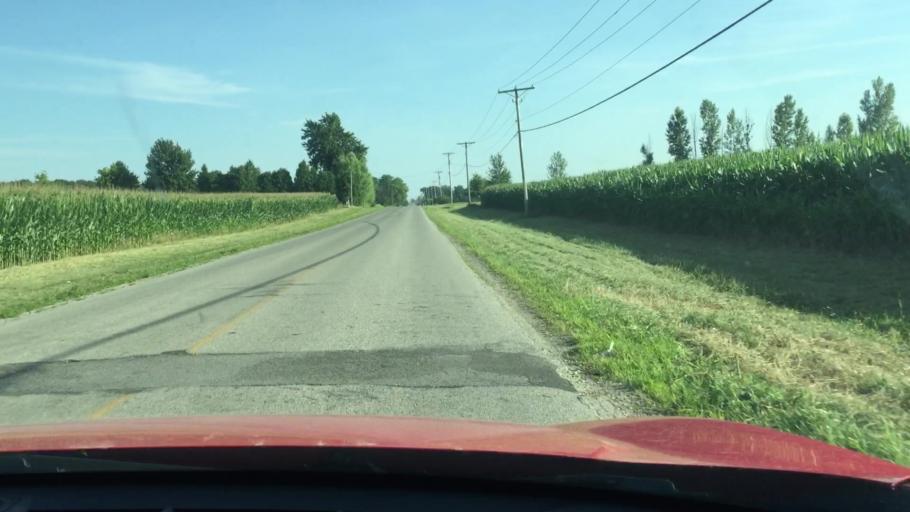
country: US
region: Ohio
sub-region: Hardin County
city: Ada
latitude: 40.7451
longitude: -83.8424
